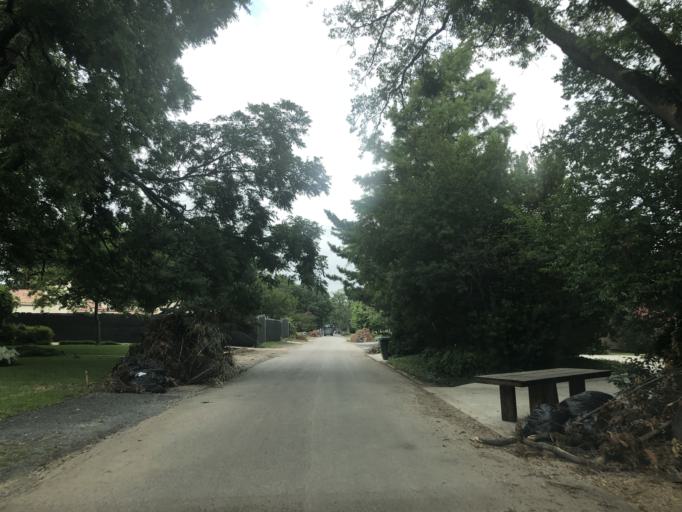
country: US
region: Texas
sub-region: Dallas County
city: University Park
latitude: 32.8536
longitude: -96.8330
